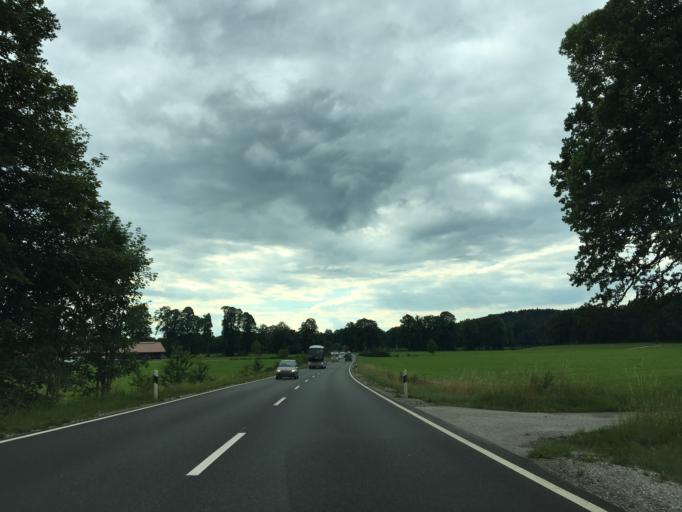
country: DE
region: Bavaria
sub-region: Upper Bavaria
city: Gmund am Tegernsee
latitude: 47.7773
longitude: 11.7434
